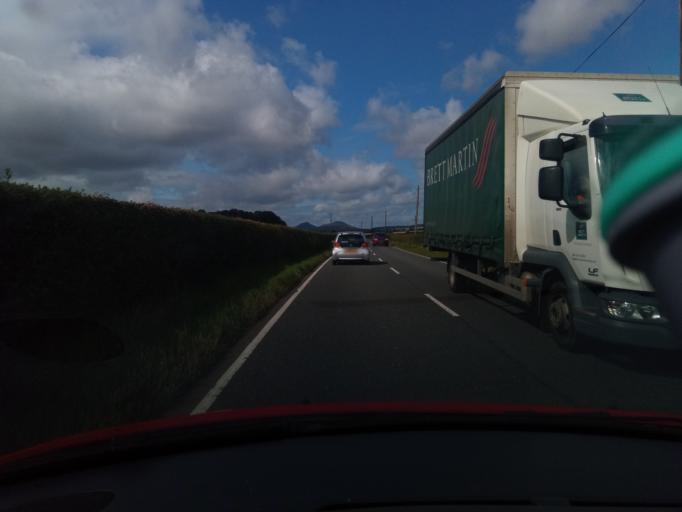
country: GB
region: Scotland
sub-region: The Scottish Borders
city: Saint Boswells
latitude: 55.5735
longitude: -2.5519
